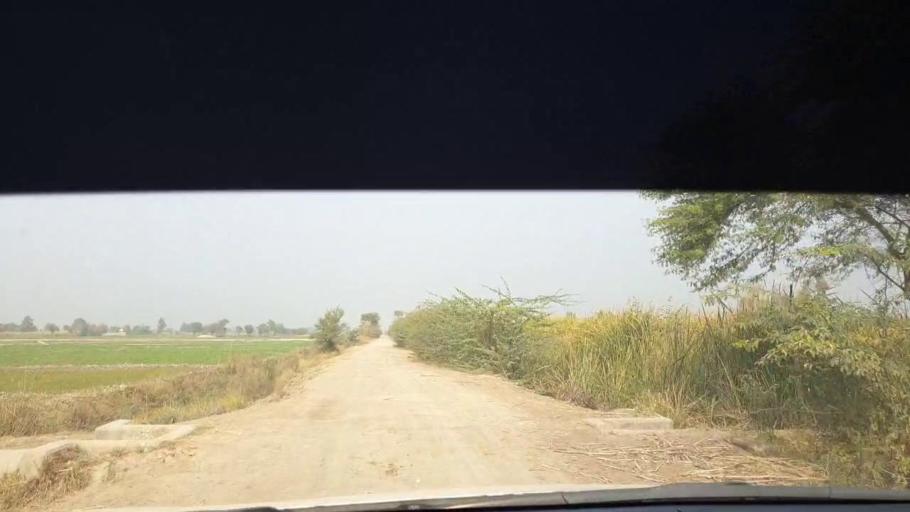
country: PK
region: Sindh
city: Berani
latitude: 25.8281
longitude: 68.8353
